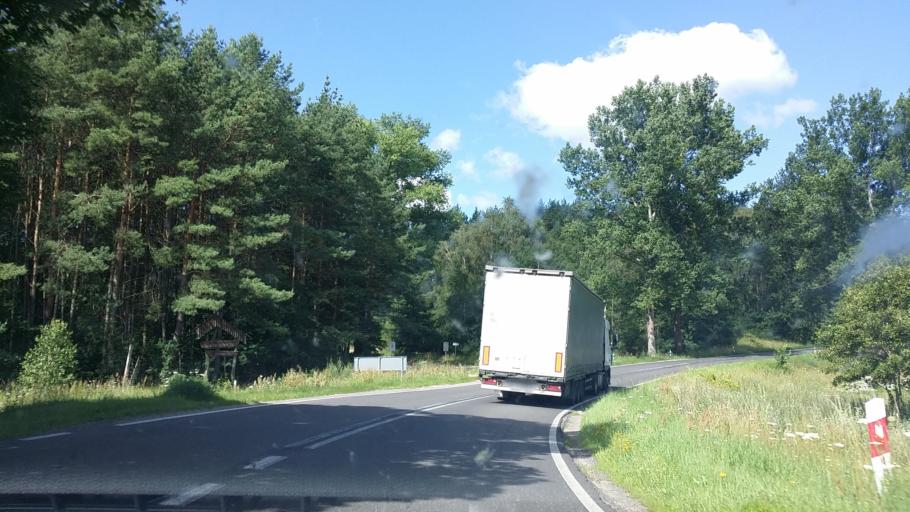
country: PL
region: West Pomeranian Voivodeship
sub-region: Powiat drawski
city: Kalisz Pomorski
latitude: 53.3709
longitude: 15.8755
